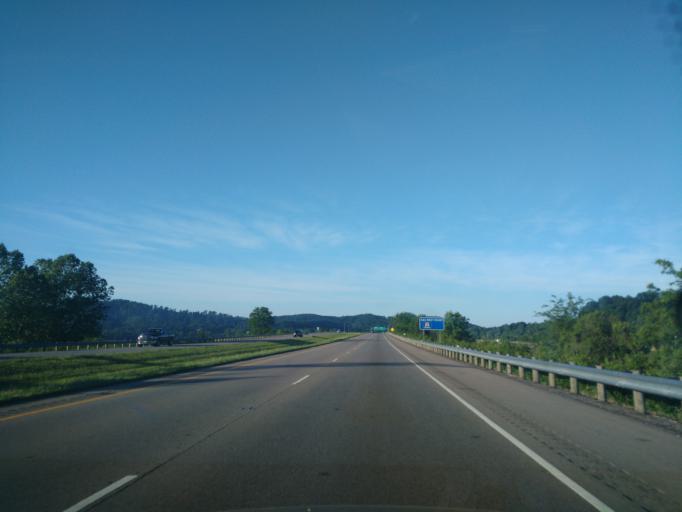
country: US
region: Ohio
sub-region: Ross County
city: Chillicothe
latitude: 39.2976
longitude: -82.9438
